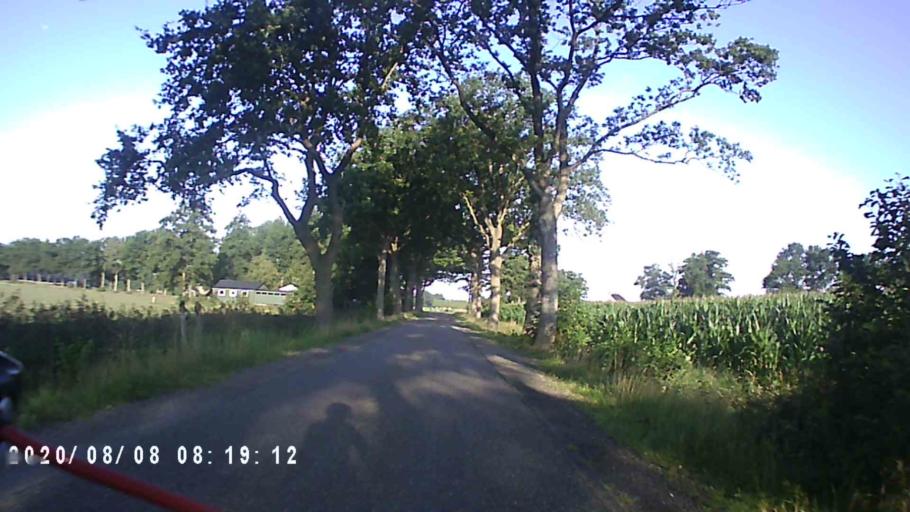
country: NL
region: Groningen
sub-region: Gemeente Leek
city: Leek
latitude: 53.0966
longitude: 6.3178
